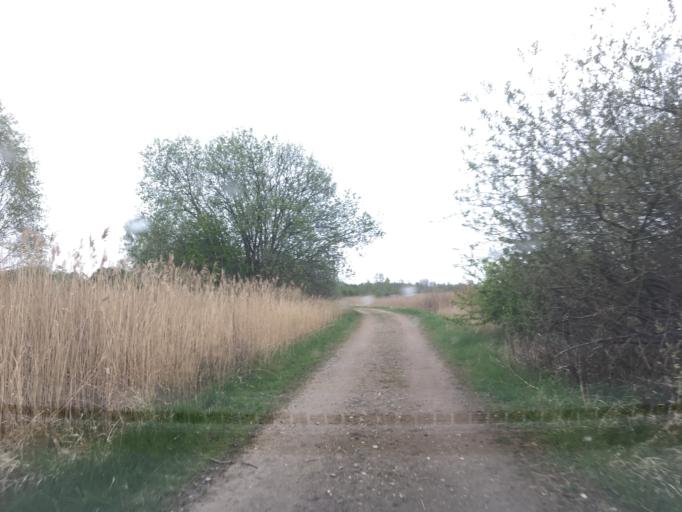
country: DK
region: Capital Region
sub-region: Tarnby Kommune
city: Tarnby
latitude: 55.5858
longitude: 12.5681
